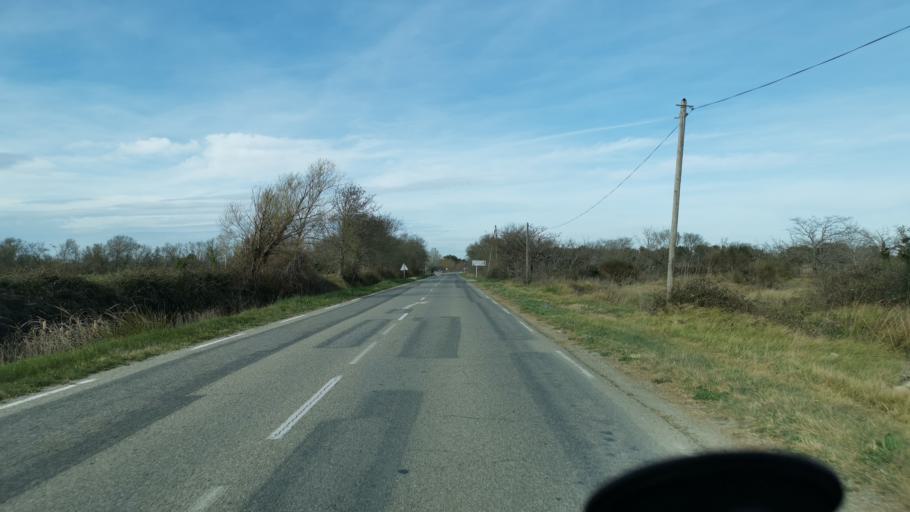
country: FR
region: Provence-Alpes-Cote d'Azur
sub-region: Departement des Bouches-du-Rhone
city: Saint-Martin-de-Crau
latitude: 43.5656
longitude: 4.7410
